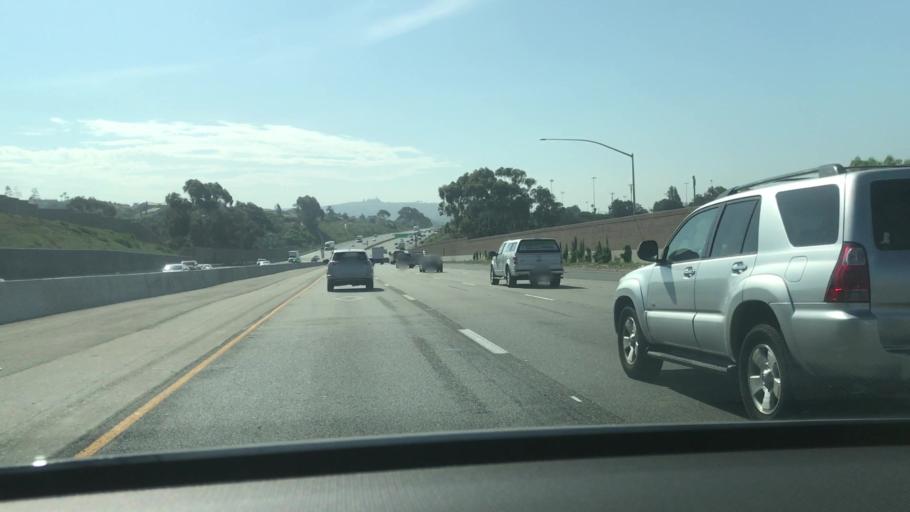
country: US
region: California
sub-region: Orange County
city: San Clemente
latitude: 33.4548
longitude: -117.6477
